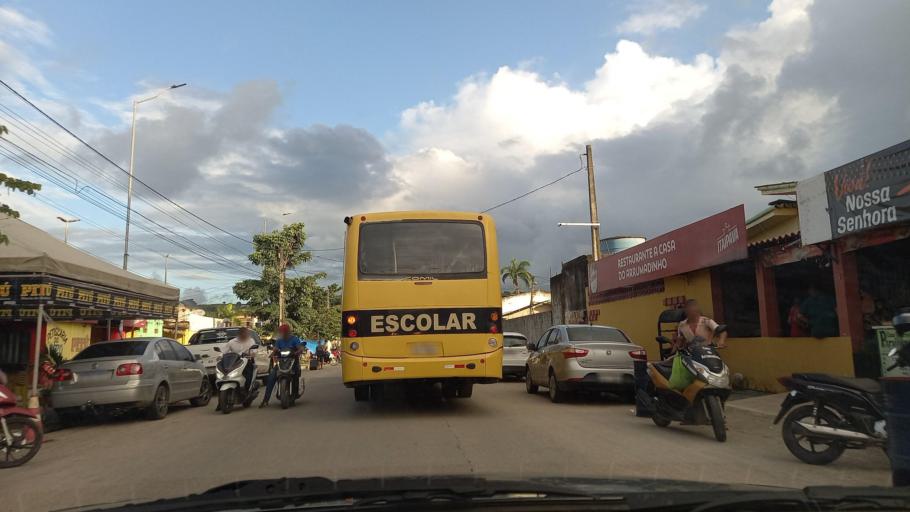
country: BR
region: Pernambuco
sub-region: Palmares
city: Palmares
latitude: -8.6858
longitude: -35.5961
